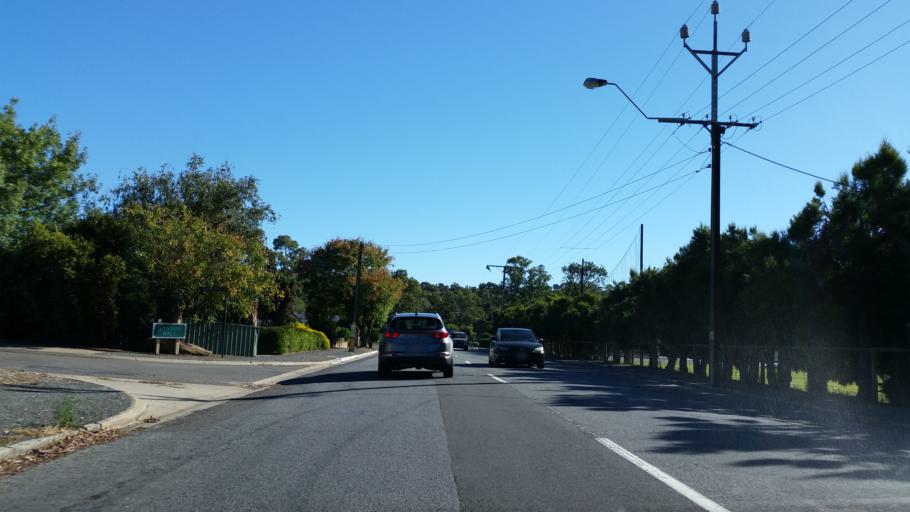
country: AU
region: South Australia
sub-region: Adelaide Hills
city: Gumeracha
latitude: -34.8215
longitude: 138.8878
